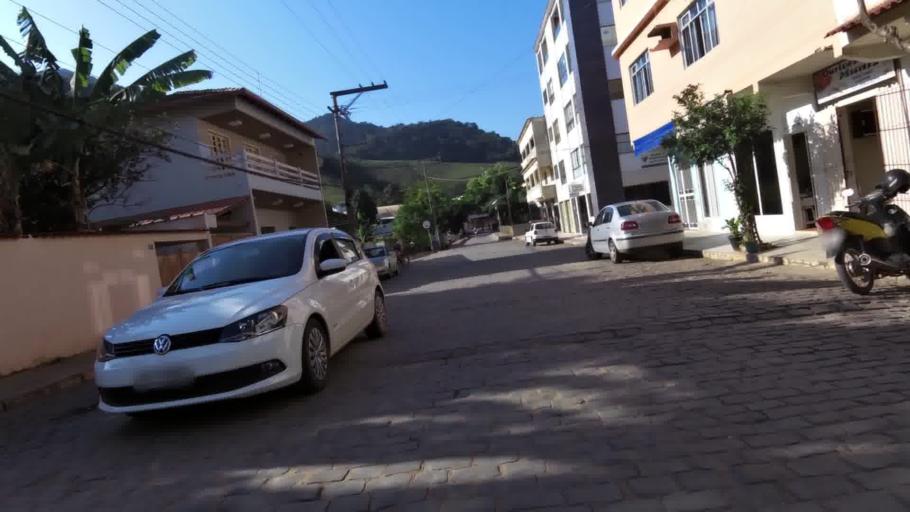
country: BR
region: Espirito Santo
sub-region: Alfredo Chaves
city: Alfredo Chaves
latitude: -20.6347
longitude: -40.7491
